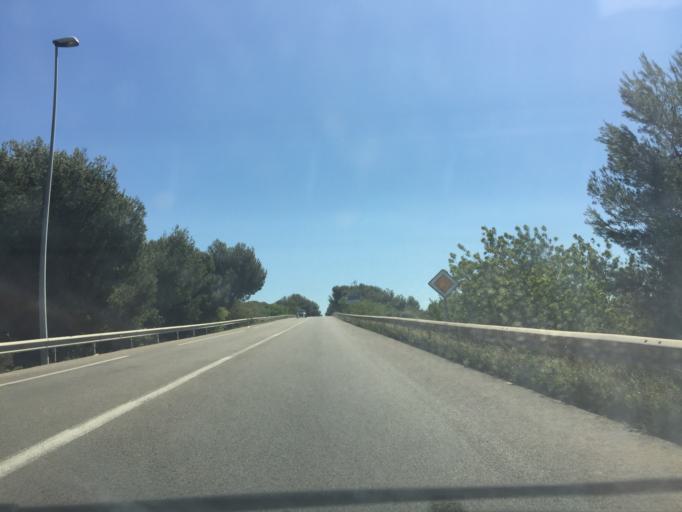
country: FR
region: Provence-Alpes-Cote d'Azur
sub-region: Departement des Bouches-du-Rhone
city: Vitrolles
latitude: 43.4572
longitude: 5.2342
